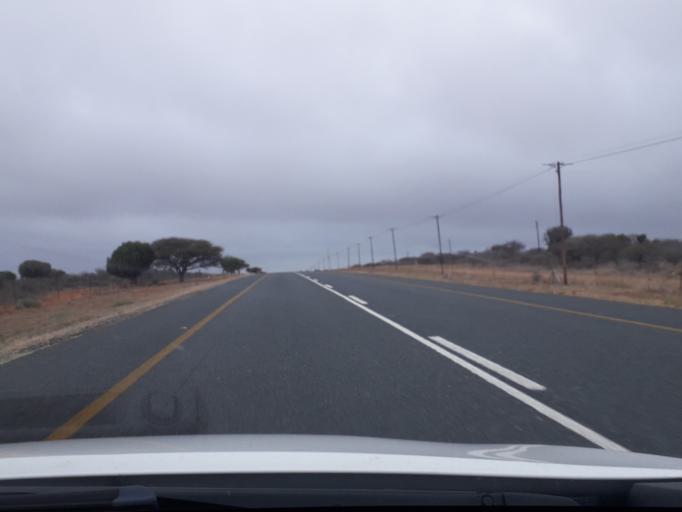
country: ZA
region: Limpopo
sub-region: Vhembe District Municipality
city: Louis Trichardt
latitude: -23.4185
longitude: 29.7527
